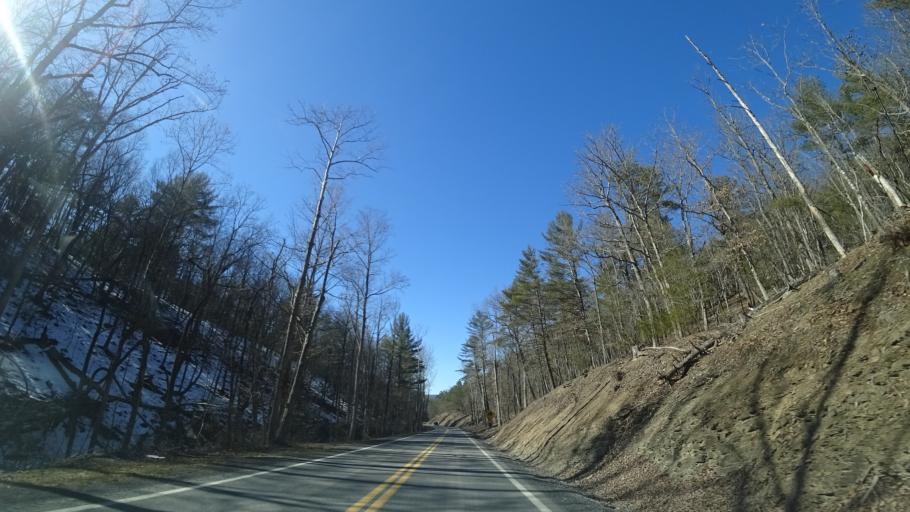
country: US
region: Virginia
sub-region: Shenandoah County
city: Woodstock
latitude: 39.0870
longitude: -78.5504
